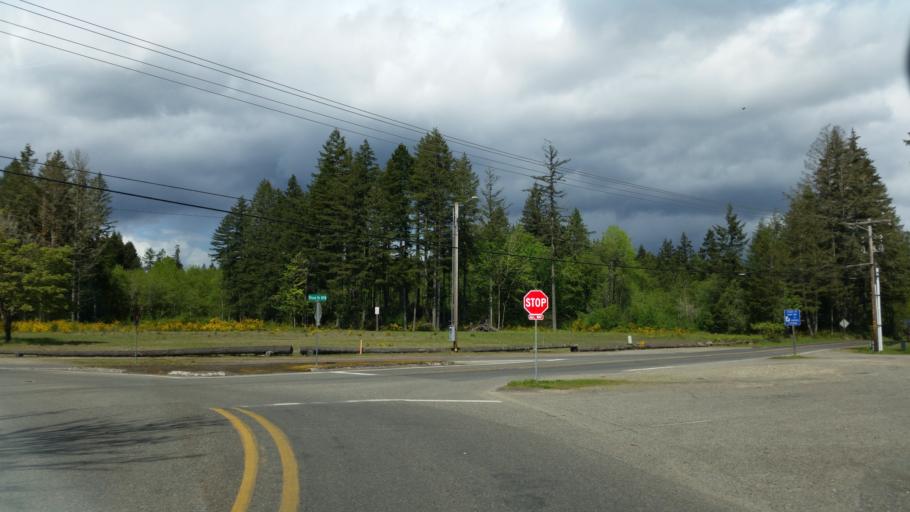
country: US
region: Washington
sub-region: Pierce County
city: Key Center
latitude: 47.3437
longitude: -122.7633
